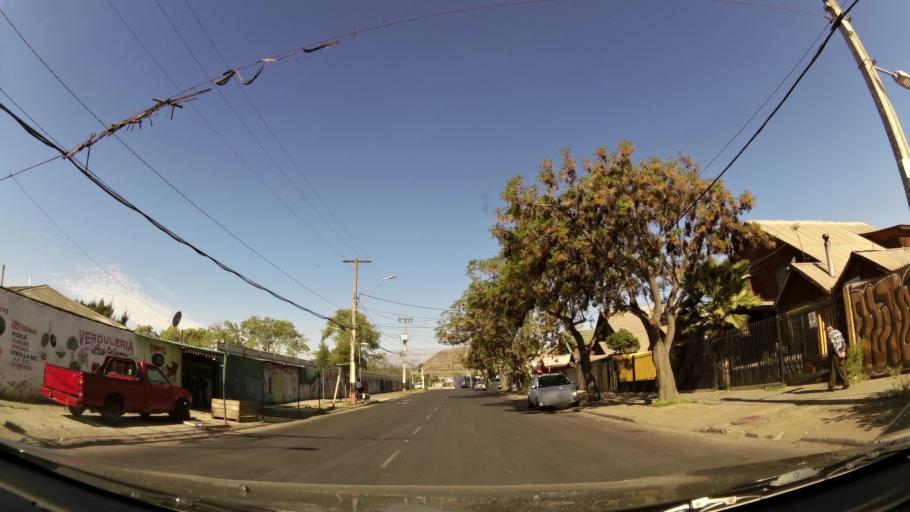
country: CL
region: Santiago Metropolitan
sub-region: Provincia de Maipo
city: San Bernardo
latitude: -33.6155
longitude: -70.6989
